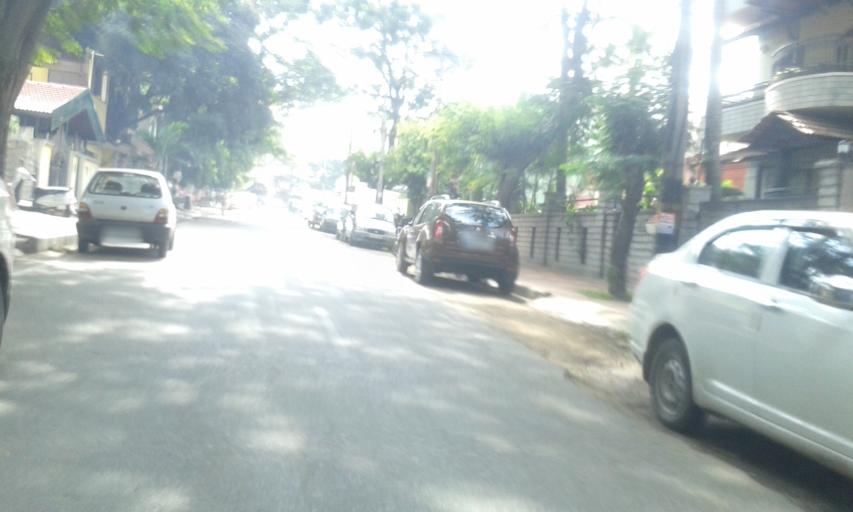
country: IN
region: Karnataka
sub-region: Bangalore Urban
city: Bangalore
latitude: 12.9457
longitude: 77.5976
